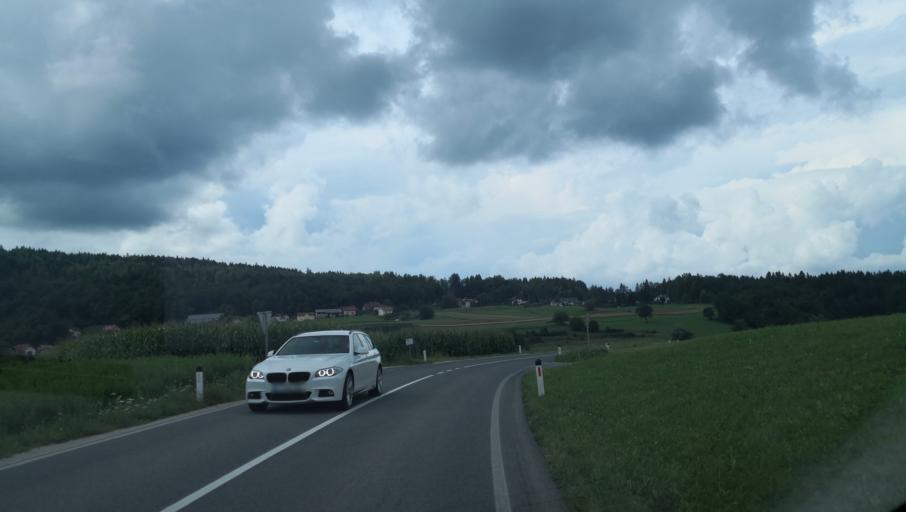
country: SI
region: Ivancna Gorica
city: Ivancna Gorica
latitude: 45.8844
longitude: 14.7915
